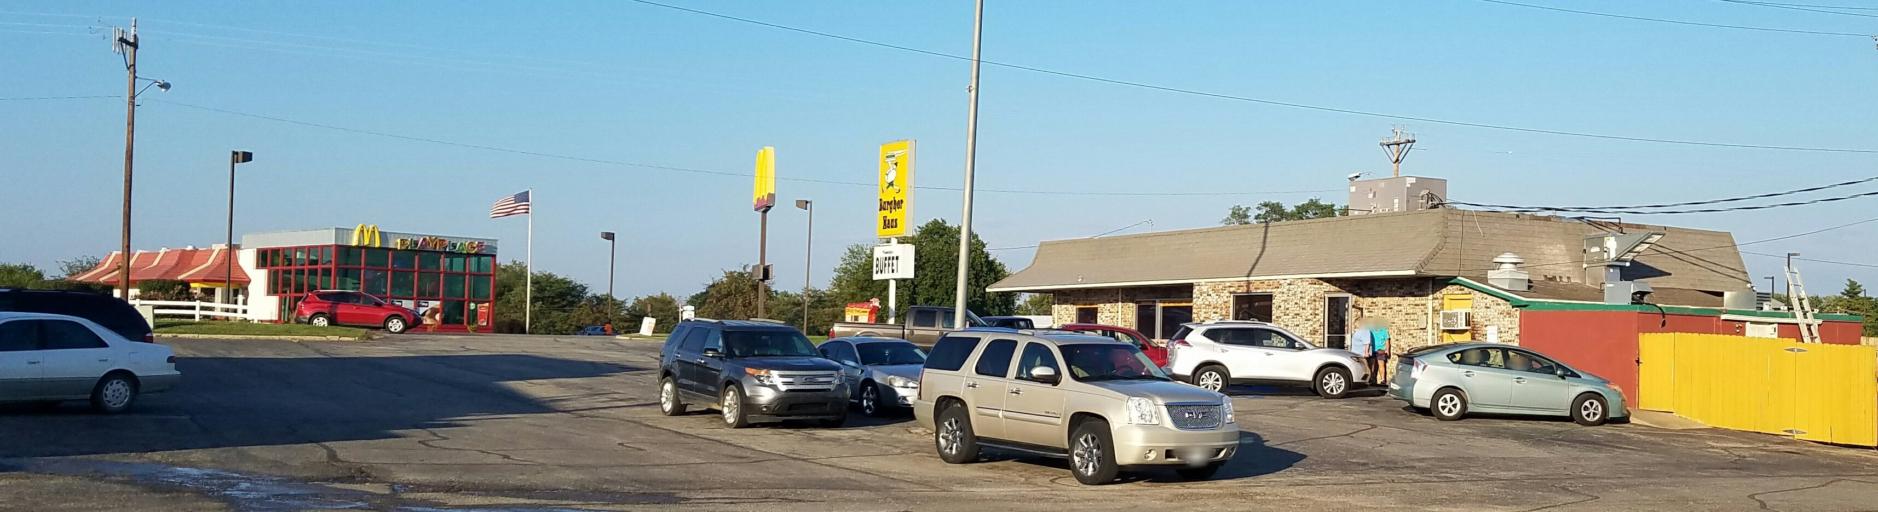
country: US
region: Missouri
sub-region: Moniteau County
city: California
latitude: 38.6297
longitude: -92.5799
